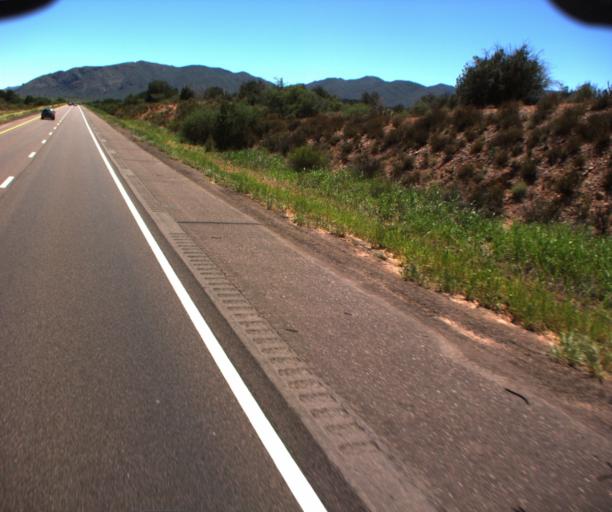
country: US
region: Arizona
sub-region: Gila County
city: Payson
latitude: 34.0716
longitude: -111.3589
